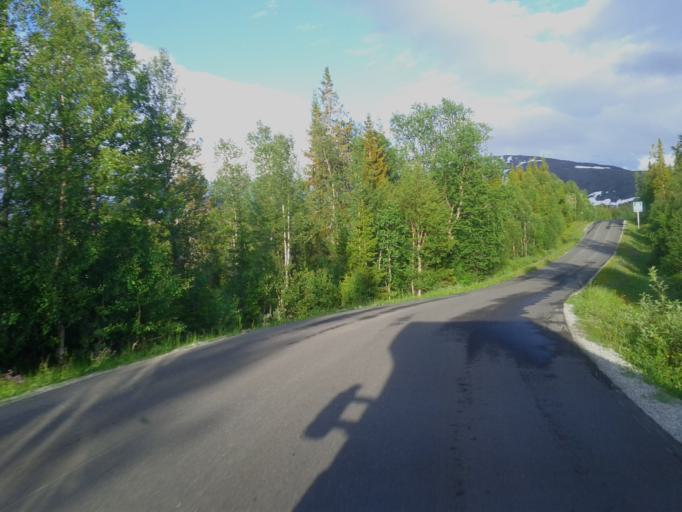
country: NO
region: Nordland
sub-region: Grane
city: Trofors
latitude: 65.4704
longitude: 13.6602
